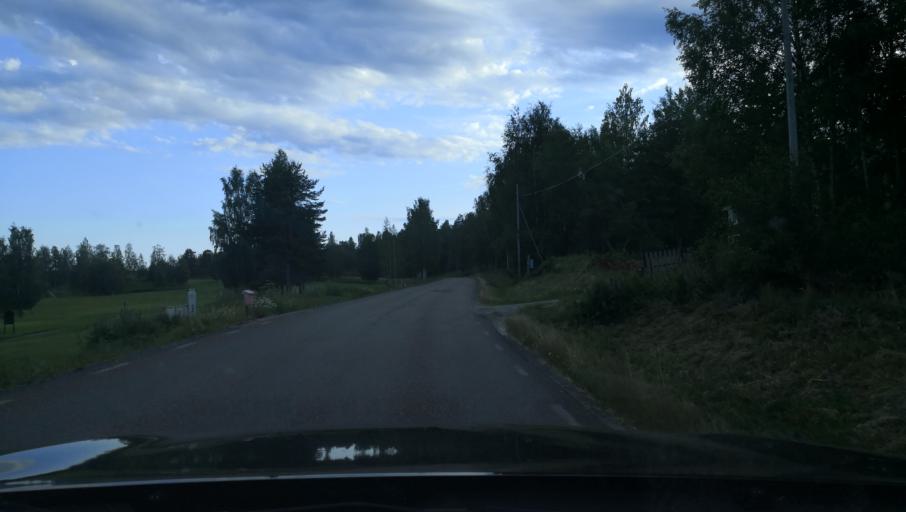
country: SE
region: Dalarna
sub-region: Ludvika Kommun
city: Ludvika
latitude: 60.1122
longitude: 15.2448
